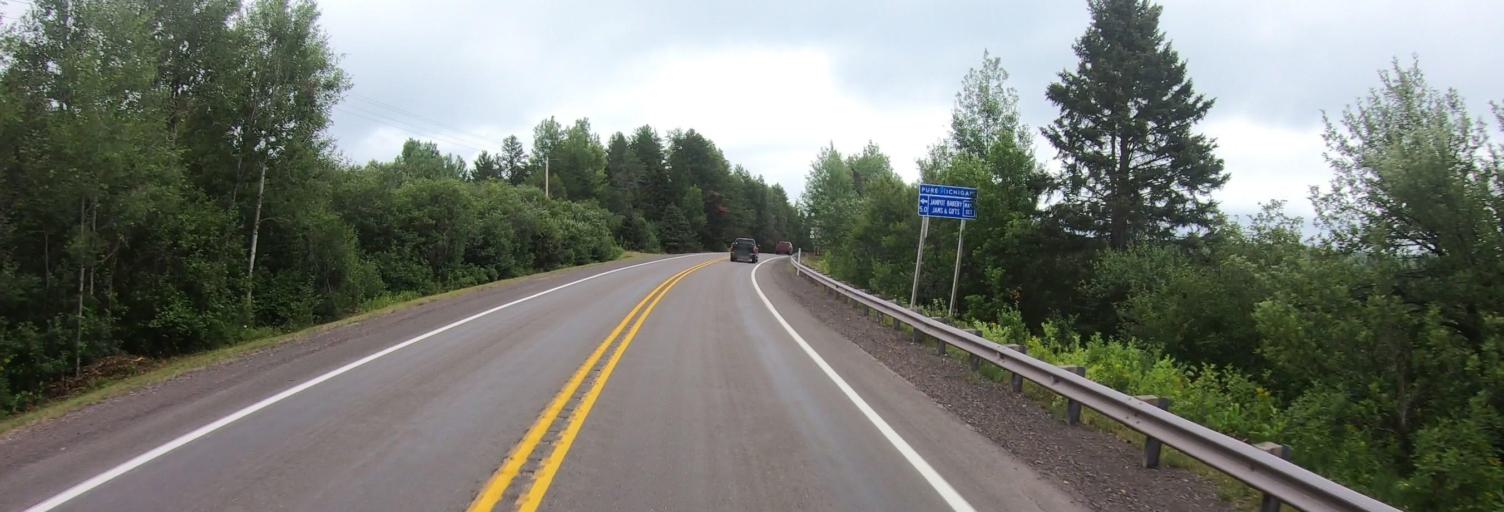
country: US
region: Michigan
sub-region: Keweenaw County
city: Eagle River
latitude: 47.3886
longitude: -88.2831
